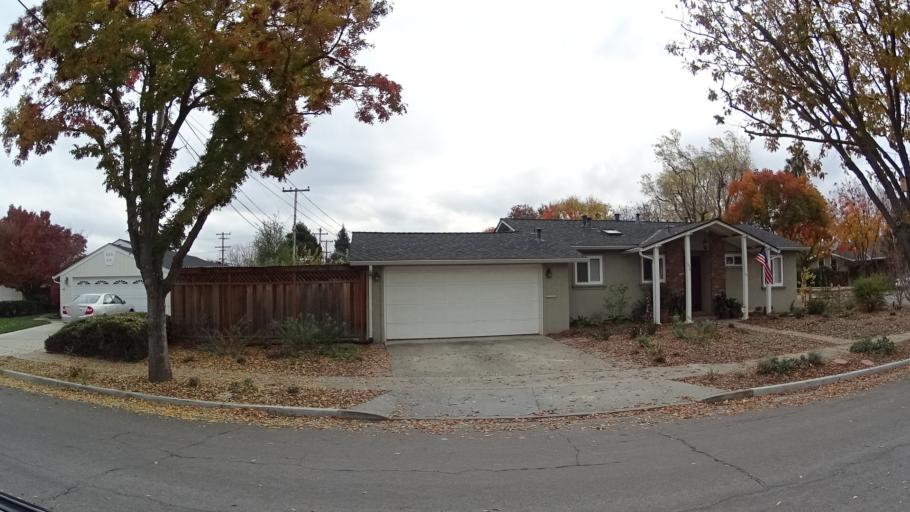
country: US
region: California
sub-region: Santa Clara County
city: Sunnyvale
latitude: 37.3661
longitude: -122.0517
